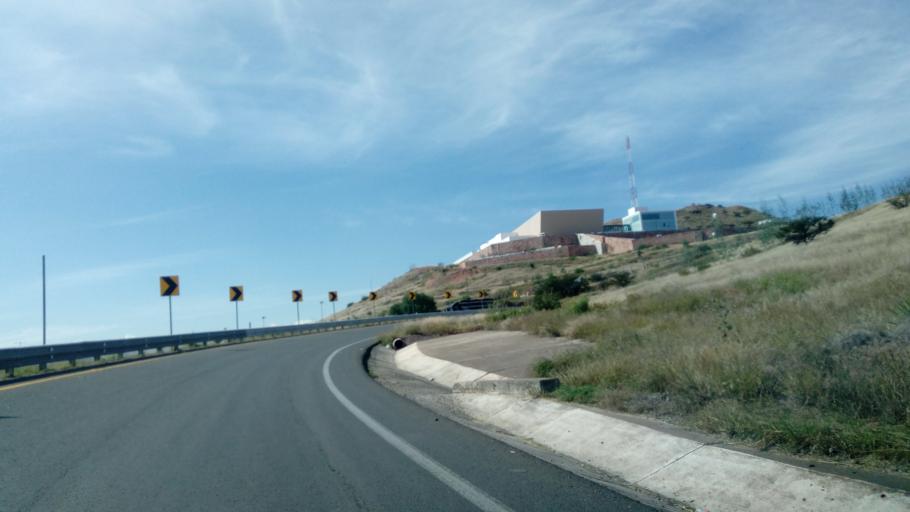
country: MX
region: Durango
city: Victoria de Durango
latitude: 24.0685
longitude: -104.6545
